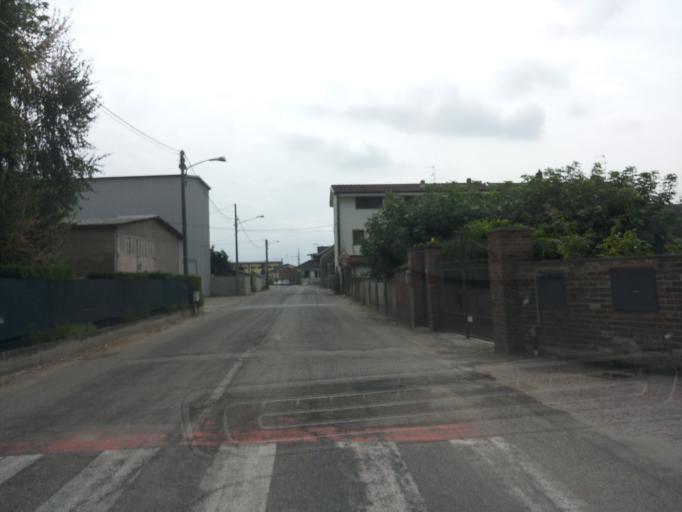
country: IT
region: Piedmont
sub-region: Provincia di Vercelli
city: Prarolo
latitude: 45.2813
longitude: 8.4803
